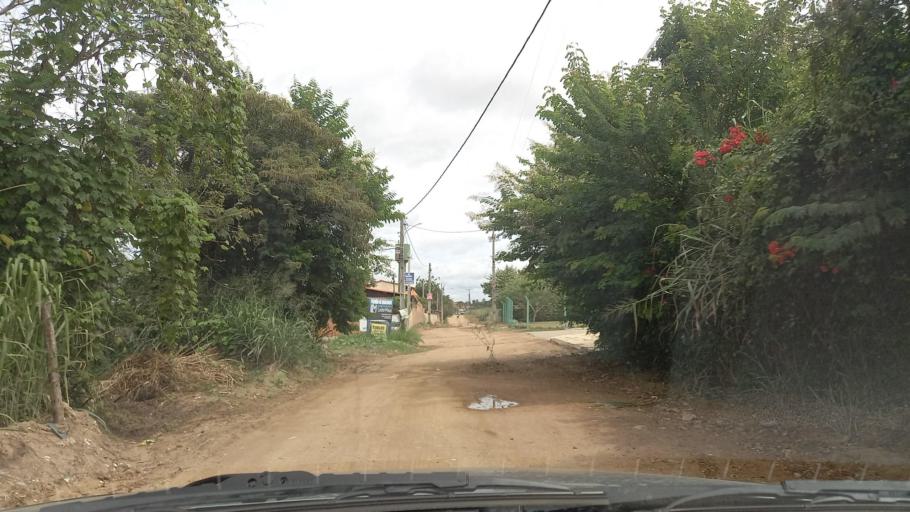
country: BR
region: Pernambuco
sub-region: Gravata
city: Gravata
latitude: -8.1916
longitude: -35.5930
